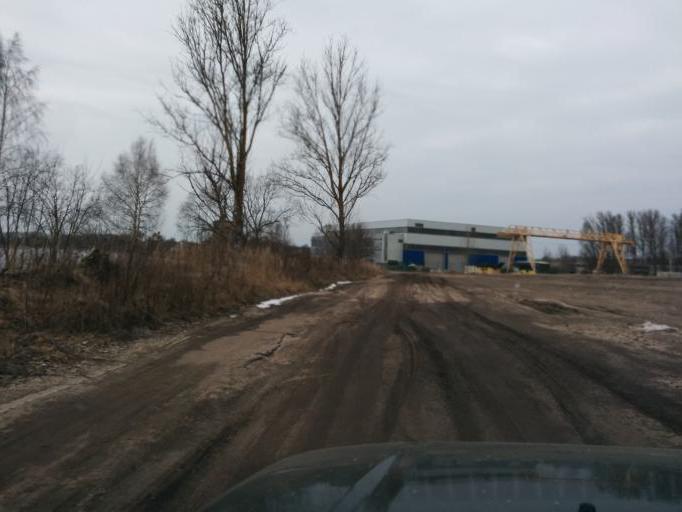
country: LV
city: Tireli
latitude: 56.9403
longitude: 23.6430
